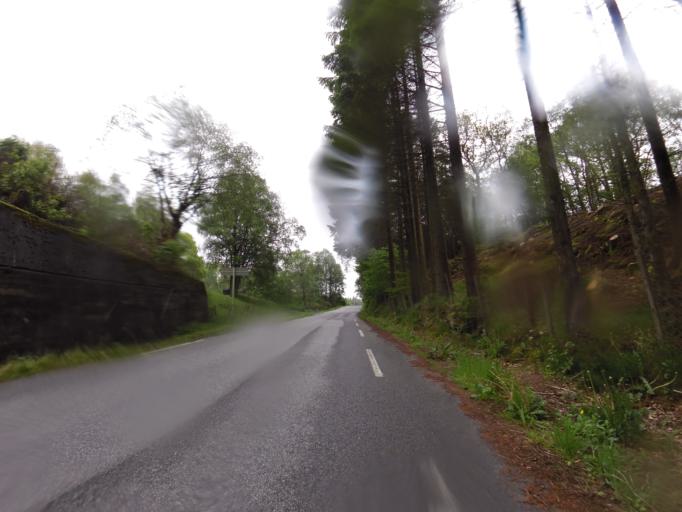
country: NO
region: Hordaland
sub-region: Sveio
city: Sveio
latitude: 59.5267
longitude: 5.2801
